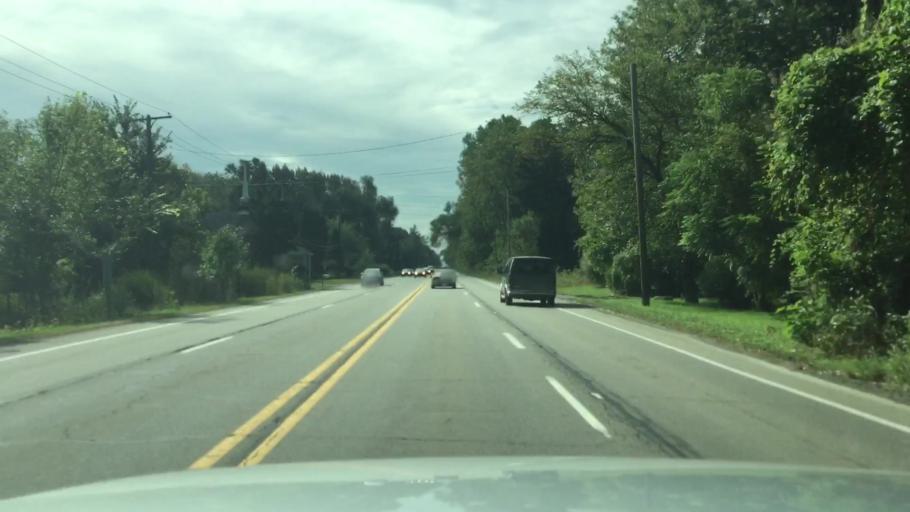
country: US
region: Michigan
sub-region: Wayne County
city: Belleville
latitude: 42.2542
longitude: -83.4866
